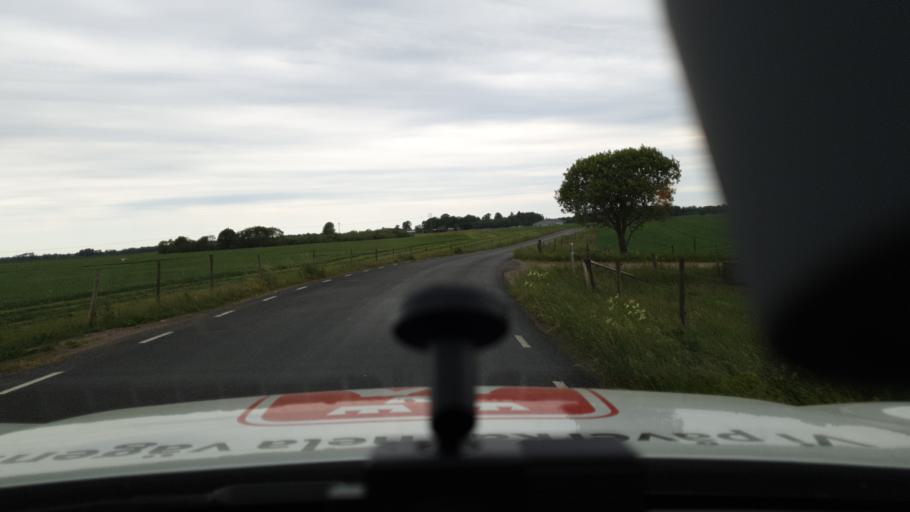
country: SE
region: Vaestra Goetaland
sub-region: Falkopings Kommun
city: Falkoeping
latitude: 58.0954
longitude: 13.4976
